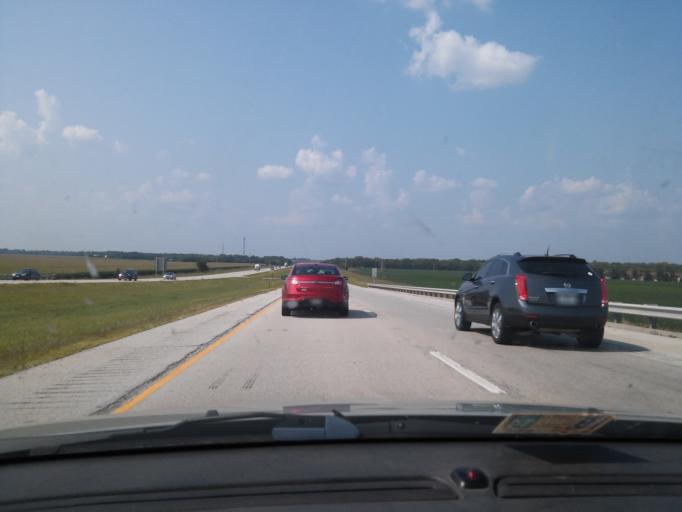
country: US
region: Illinois
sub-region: Livingston County
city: Pontiac
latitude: 40.8827
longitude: -88.6713
